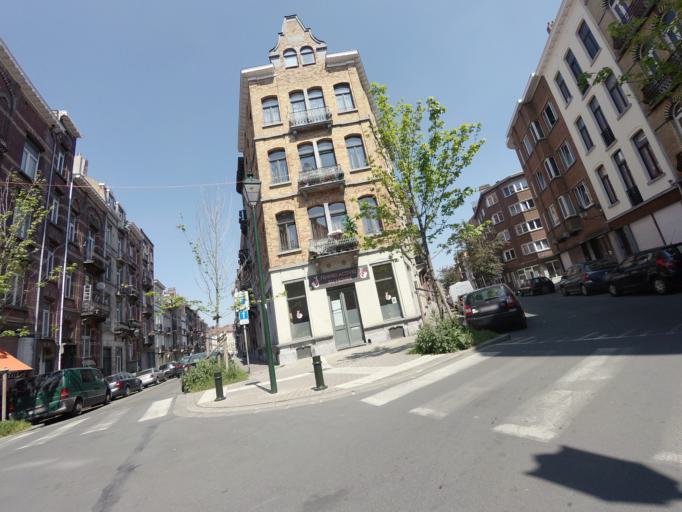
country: BE
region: Brussels Capital
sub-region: Bruxelles-Capitale
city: Brussels
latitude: 50.8269
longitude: 4.3358
